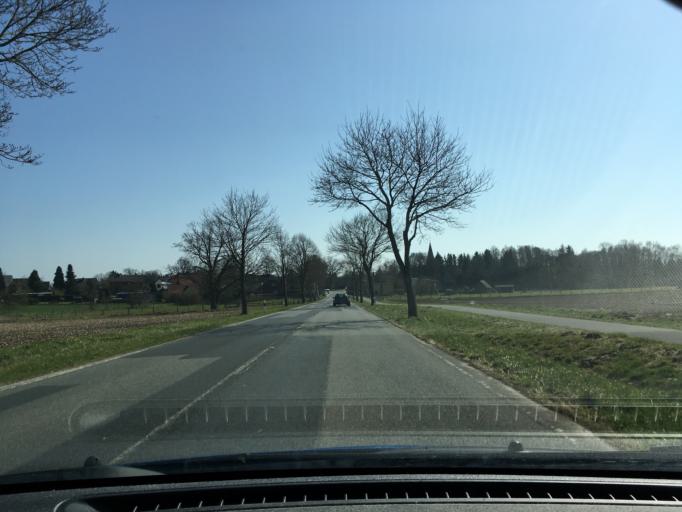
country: DE
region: Lower Saxony
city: Wriedel
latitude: 53.0373
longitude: 10.2981
